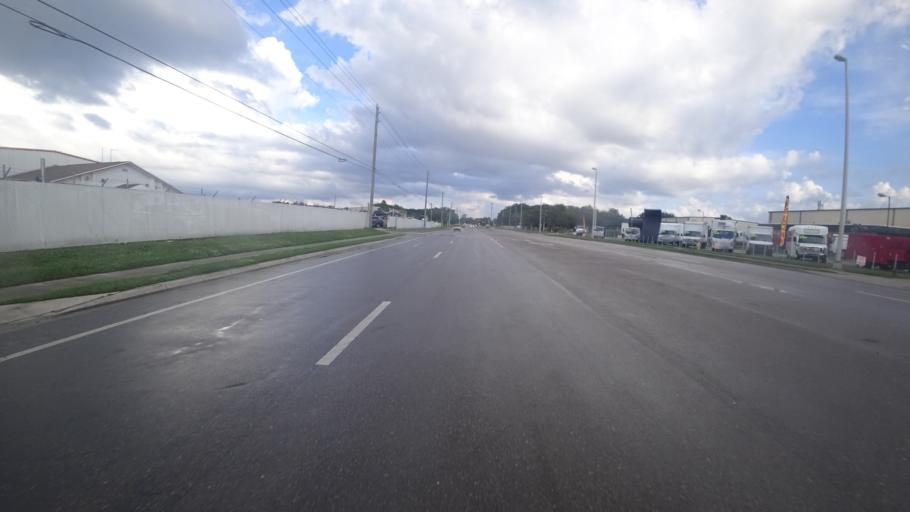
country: US
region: Florida
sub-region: Manatee County
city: Memphis
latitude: 27.5284
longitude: -82.5522
